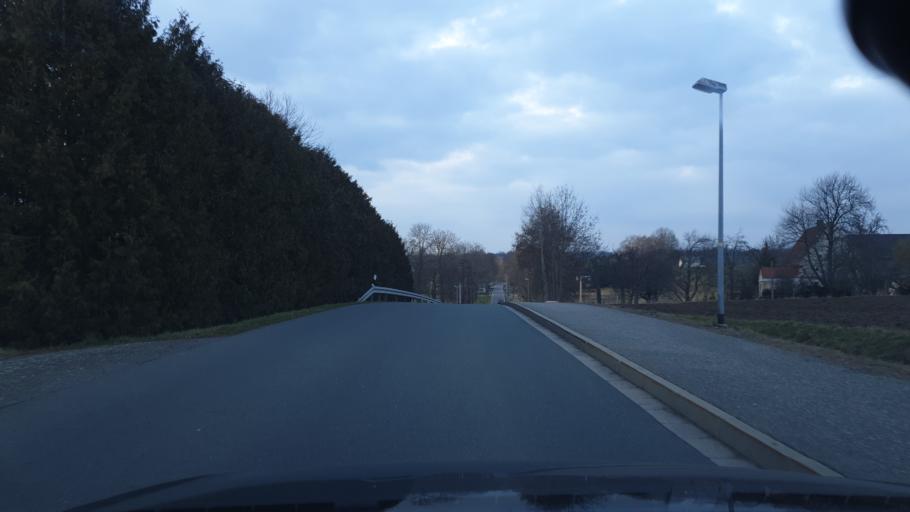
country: DE
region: Saxony
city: Erlau
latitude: 50.9921
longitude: 12.9132
